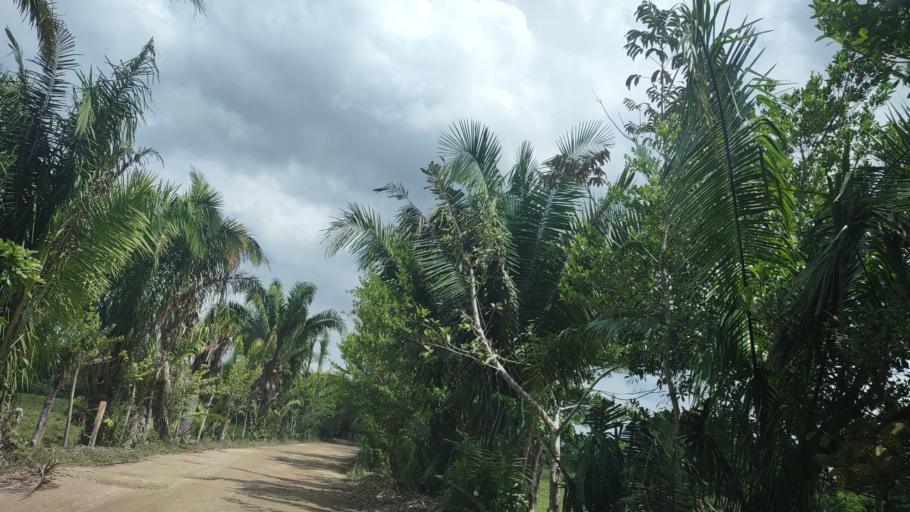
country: MX
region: Veracruz
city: Las Choapas
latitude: 17.9628
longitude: -94.1234
